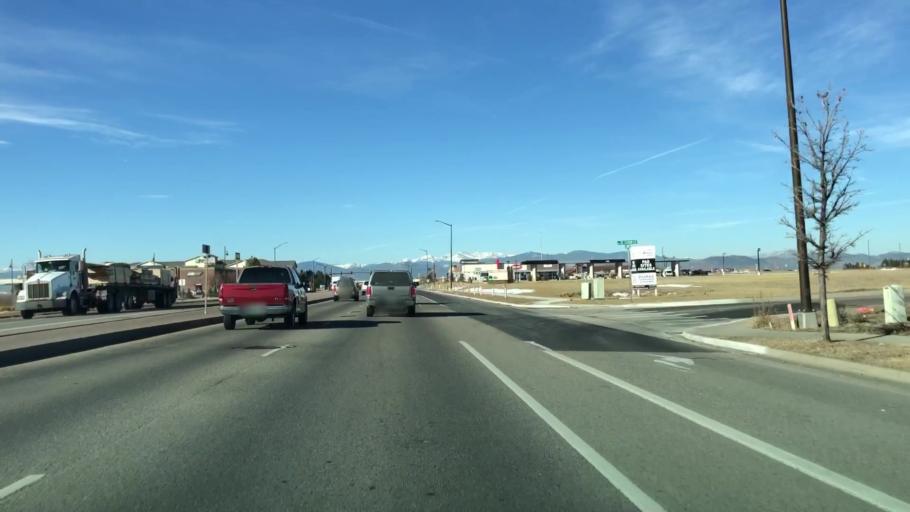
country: US
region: Colorado
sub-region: Weld County
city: Windsor
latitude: 40.4365
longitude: -104.9850
